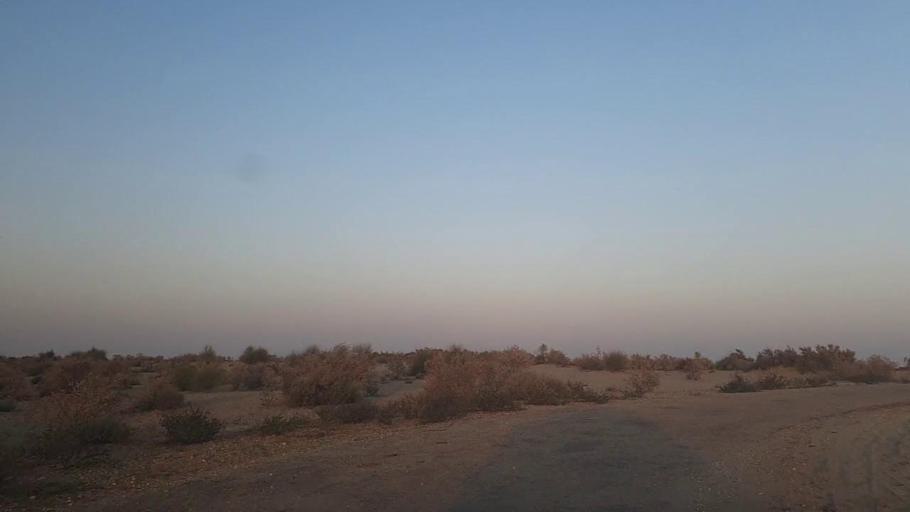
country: PK
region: Sindh
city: Jam Sahib
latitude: 26.3843
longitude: 68.6913
